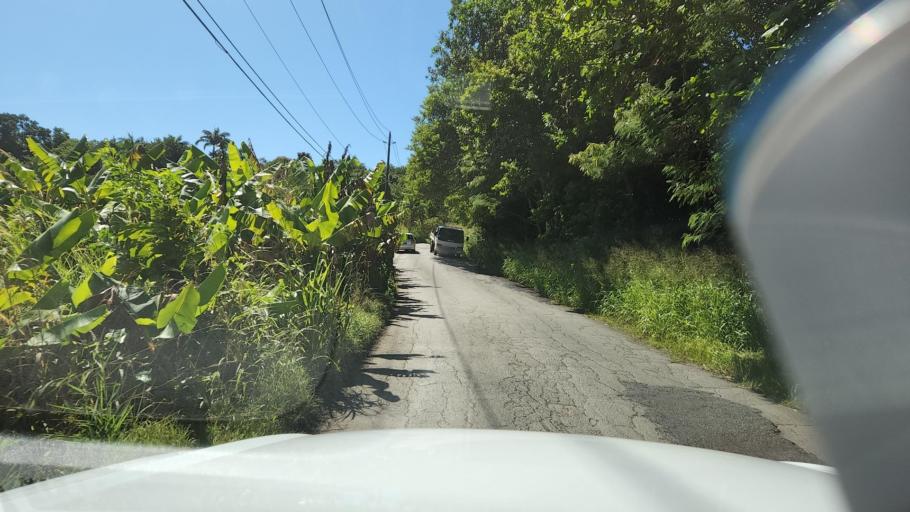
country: BB
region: Saint Thomas
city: Welchman Hall
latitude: 13.1975
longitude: -59.5674
